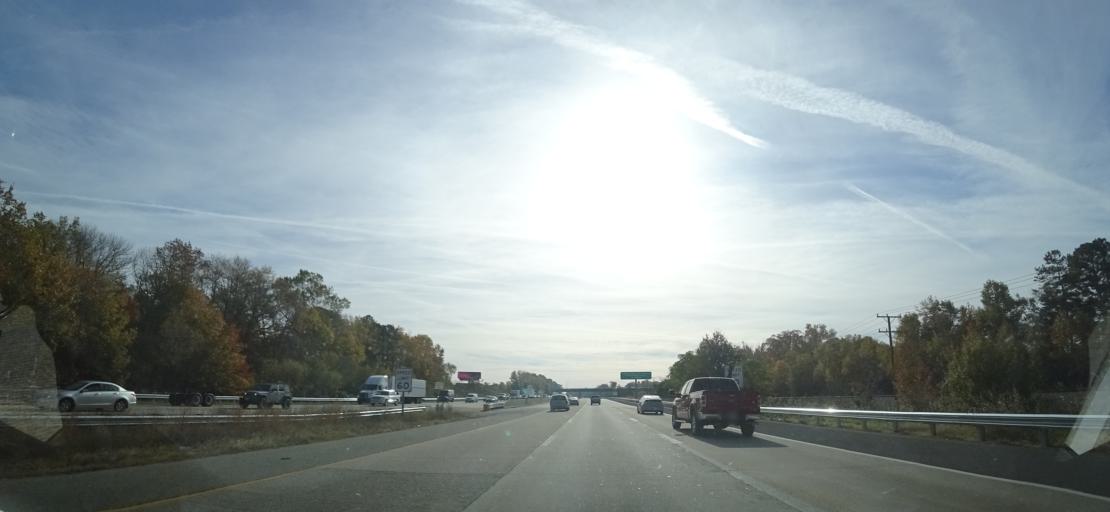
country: US
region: Virginia
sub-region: York County
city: Yorktown
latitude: 37.1283
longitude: -76.5205
